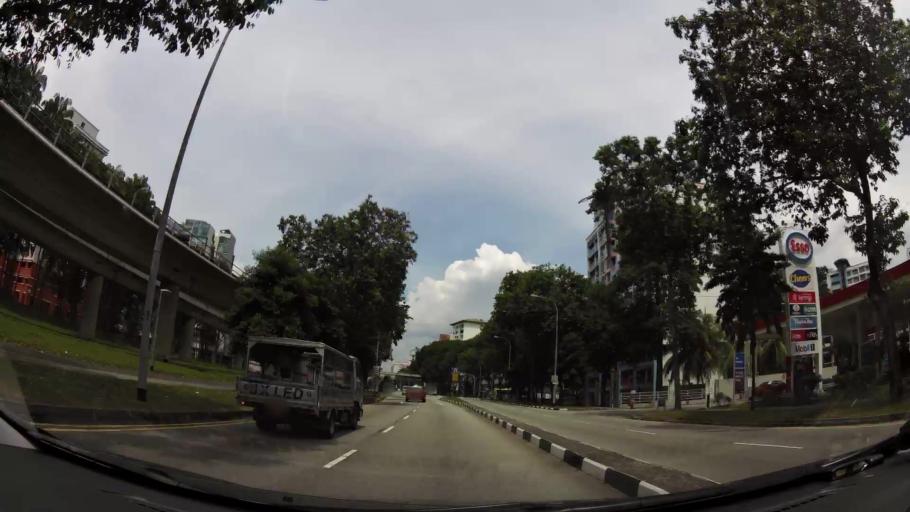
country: MY
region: Johor
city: Johor Bahru
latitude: 1.3954
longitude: 103.7471
